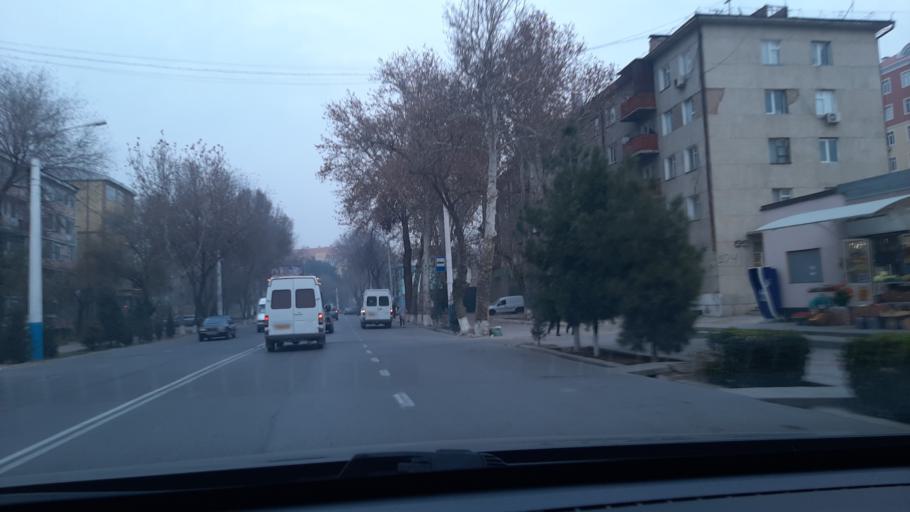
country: TJ
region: Viloyati Sughd
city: Khujand
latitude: 40.2796
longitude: 69.6154
